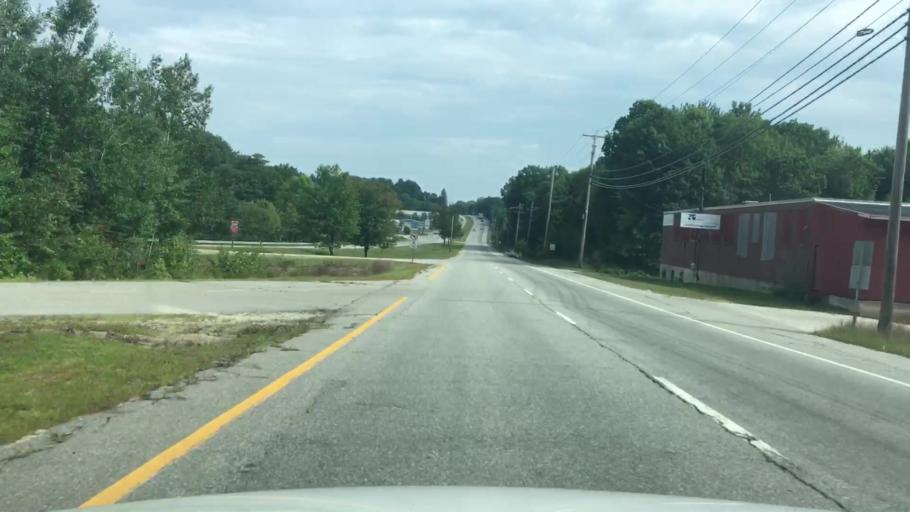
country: US
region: Maine
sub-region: Androscoggin County
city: Auburn
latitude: 44.0777
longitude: -70.2383
